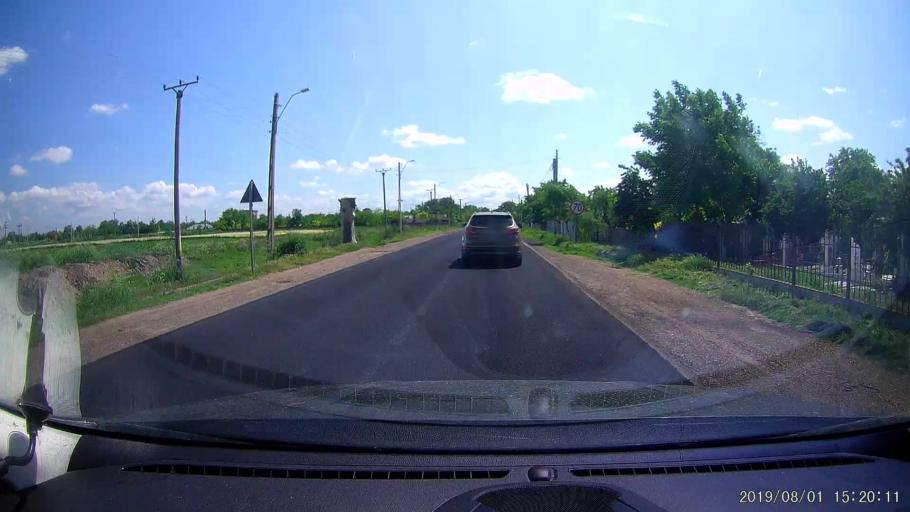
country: RO
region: Braila
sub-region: Comuna Tufesti
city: Tufesti
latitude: 45.0814
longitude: 27.8084
